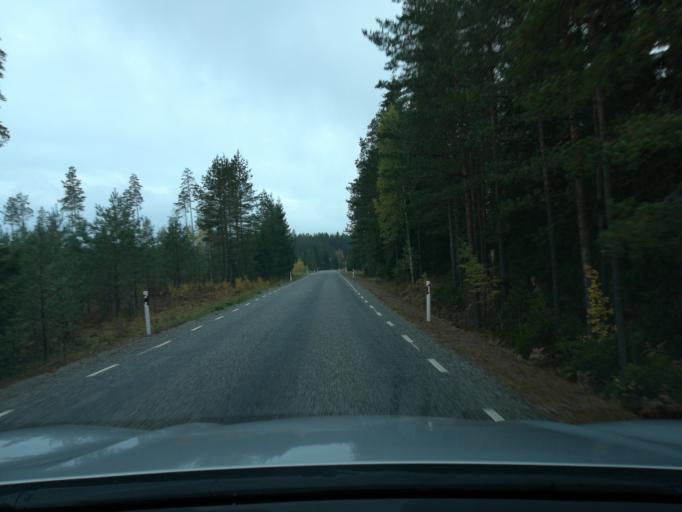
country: EE
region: Ida-Virumaa
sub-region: Johvi vald
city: Johvi
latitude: 59.1724
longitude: 27.4505
